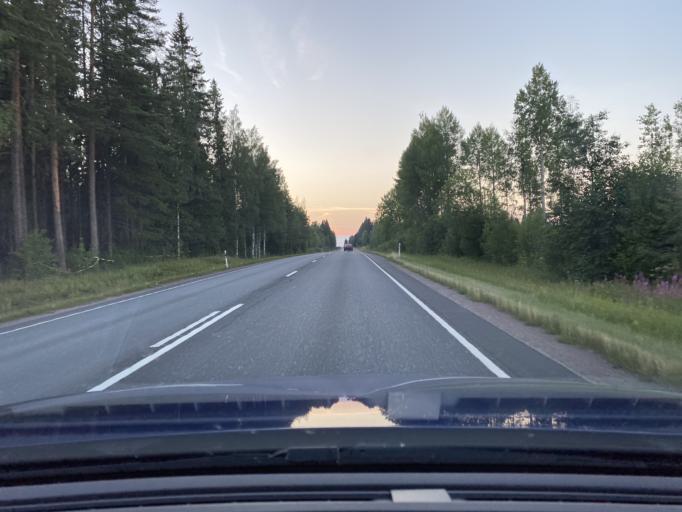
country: FI
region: Pirkanmaa
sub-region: Luoteis-Pirkanmaa
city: Ikaalinen
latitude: 61.8321
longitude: 22.9416
